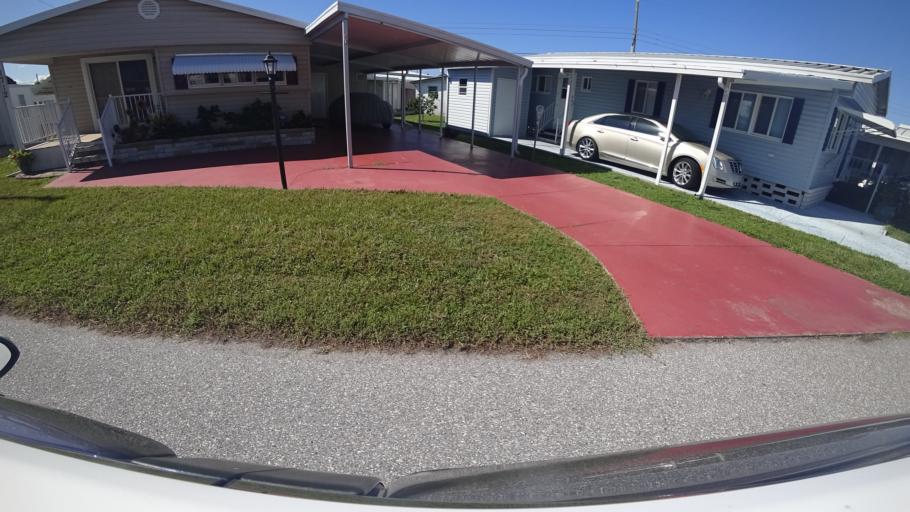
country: US
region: Florida
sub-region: Manatee County
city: Bayshore Gardens
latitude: 27.4223
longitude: -82.5791
